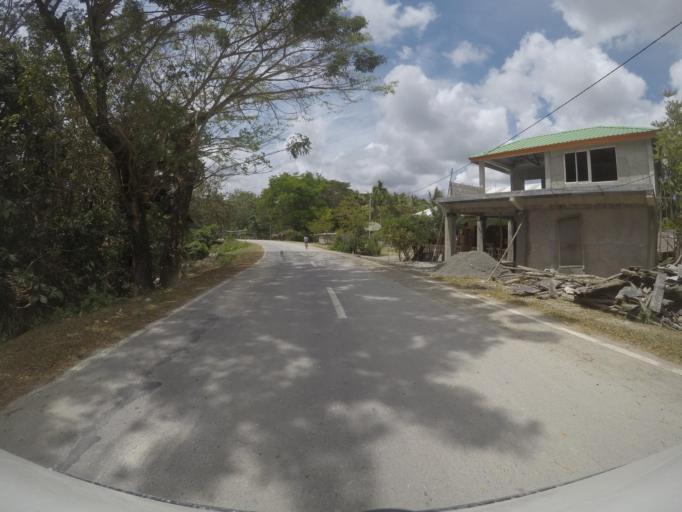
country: TL
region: Viqueque
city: Viqueque
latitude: -8.8833
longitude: 126.3764
